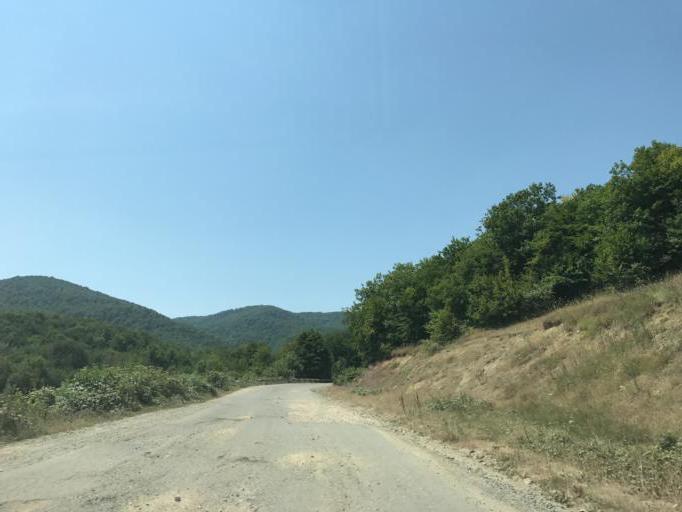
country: AZ
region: Tartar Rayon
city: Martakert
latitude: 40.1035
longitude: 46.6568
